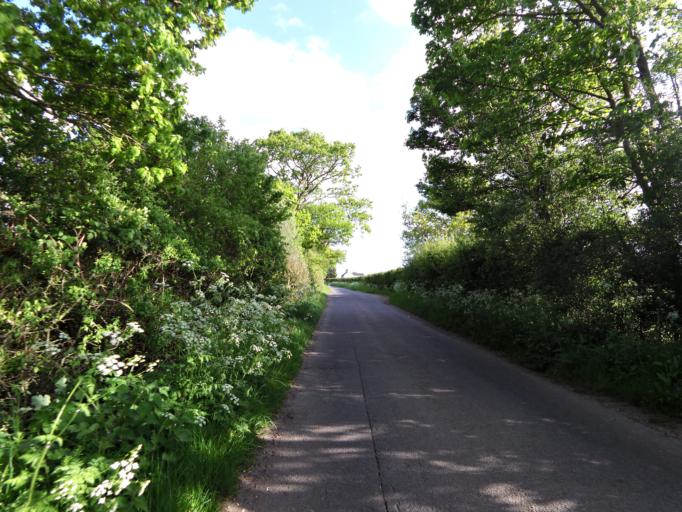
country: GB
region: England
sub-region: Suffolk
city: Halesworth
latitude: 52.4173
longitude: 1.5058
